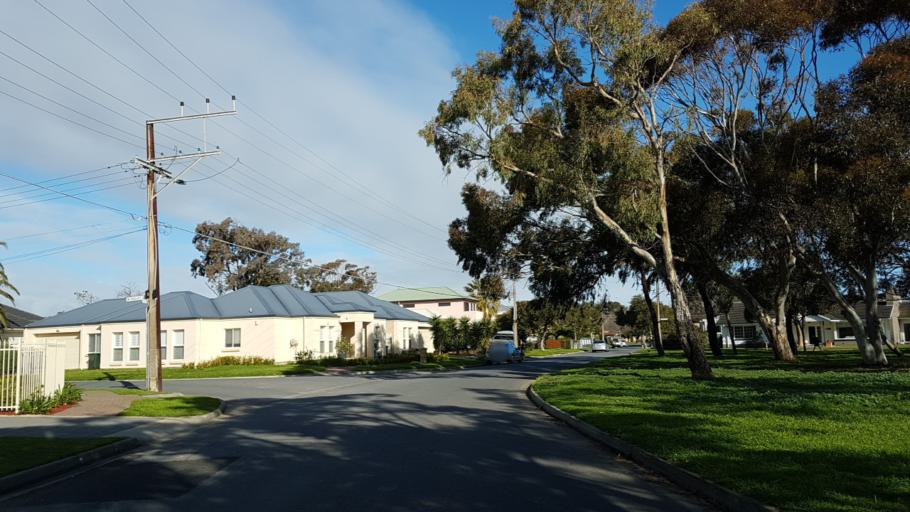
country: AU
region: South Australia
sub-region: Charles Sturt
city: Henley Beach
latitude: -34.9309
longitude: 138.5026
